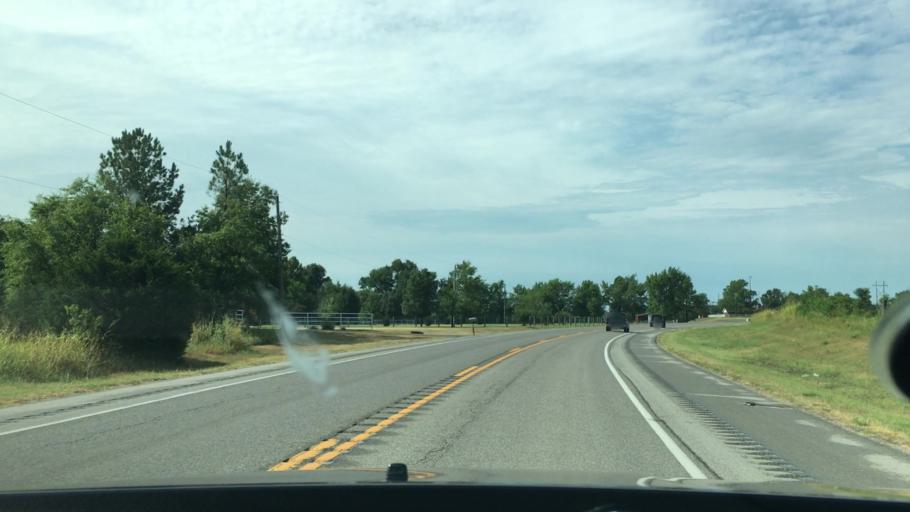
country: US
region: Oklahoma
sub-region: Murray County
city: Sulphur
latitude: 34.5323
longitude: -96.9674
